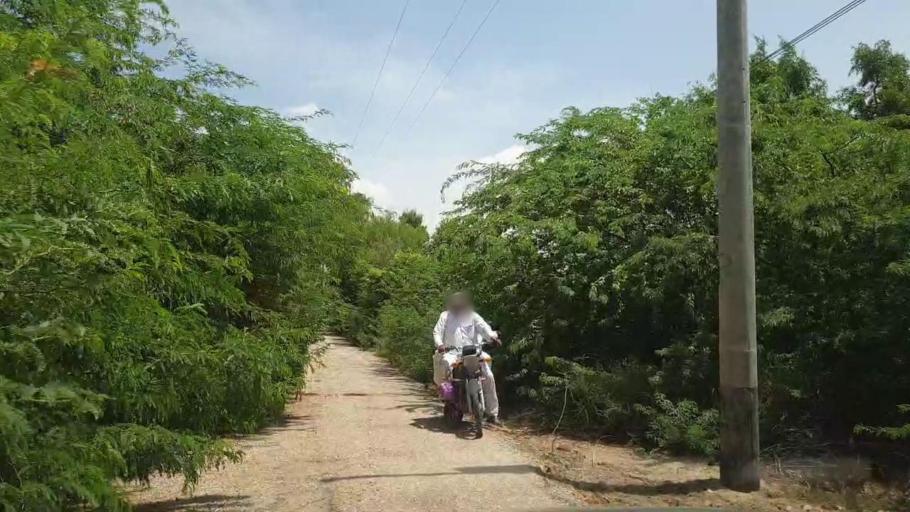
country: PK
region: Sindh
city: Kot Diji
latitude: 27.1376
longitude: 69.0092
